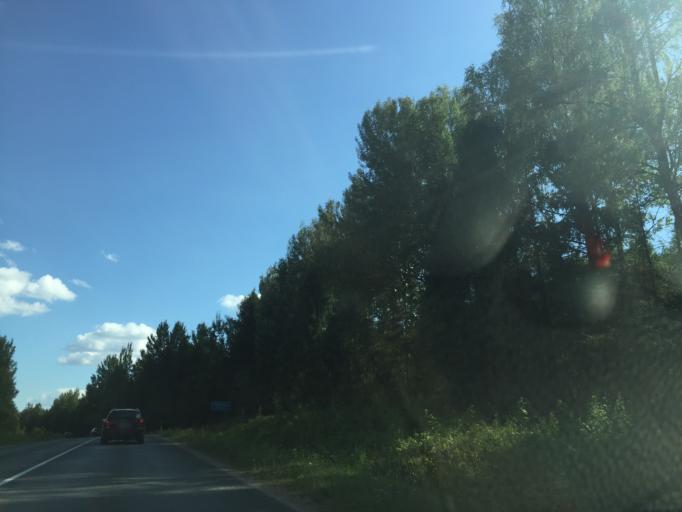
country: LV
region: Beverina
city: Murmuiza
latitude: 57.4460
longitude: 25.4316
